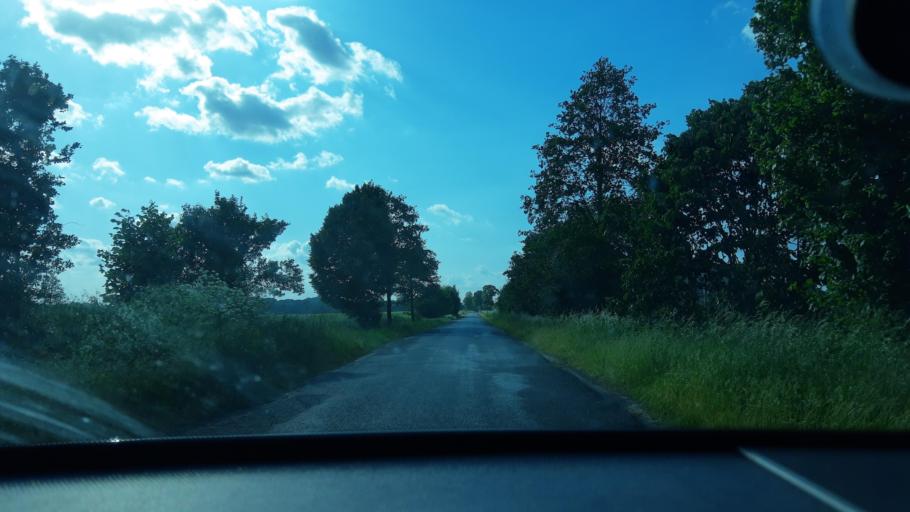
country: PL
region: Lodz Voivodeship
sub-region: Powiat zdunskowolski
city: Zapolice
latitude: 51.5354
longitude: 18.8332
